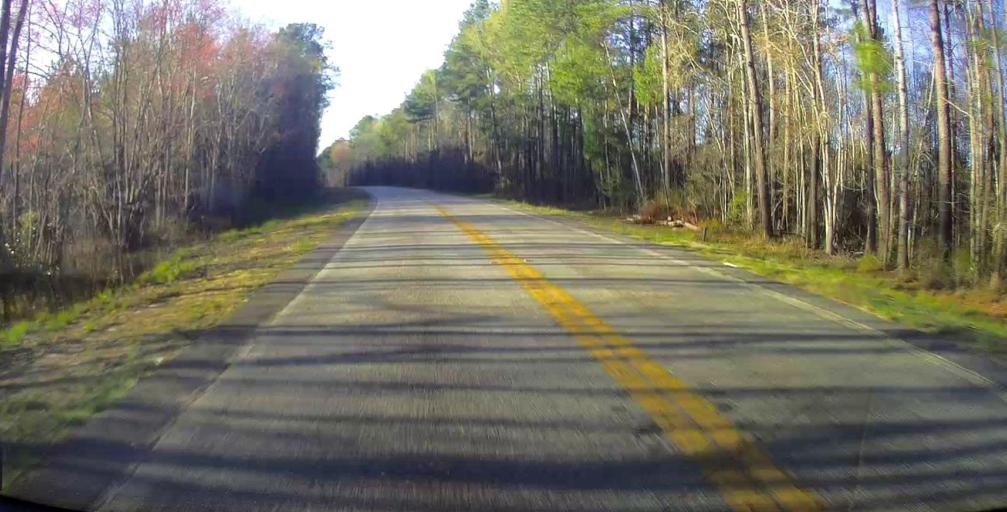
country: US
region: Georgia
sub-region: Wilcox County
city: Abbeville
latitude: 32.0875
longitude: -83.2927
